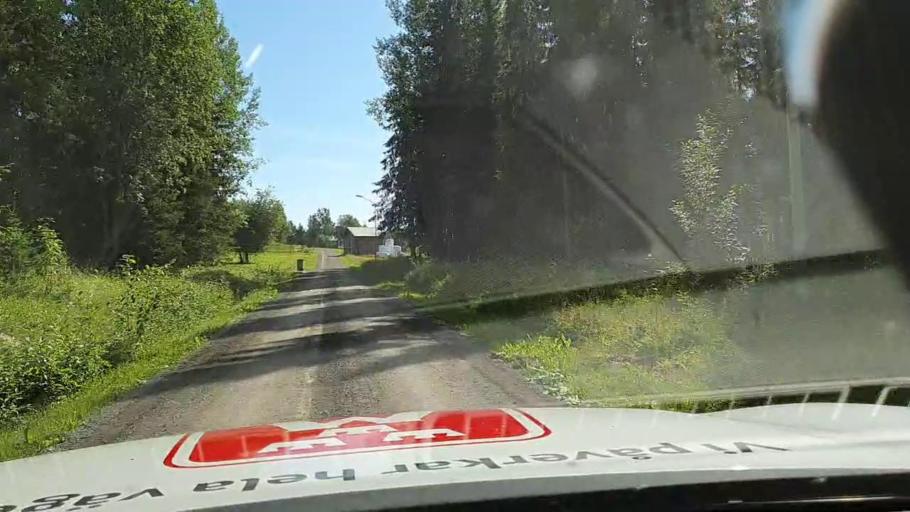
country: SE
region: Jaemtland
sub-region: Stroemsunds Kommun
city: Stroemsund
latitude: 63.7713
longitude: 15.3252
